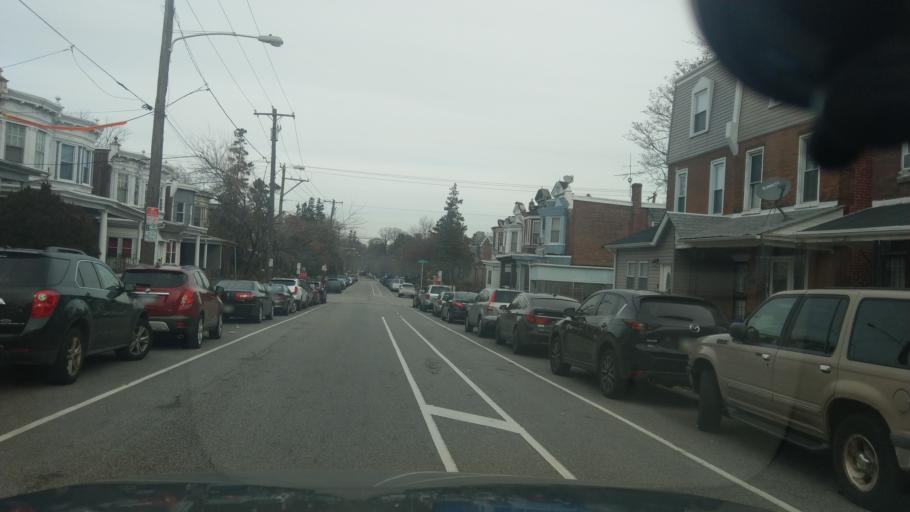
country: US
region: Pennsylvania
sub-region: Montgomery County
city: Wyncote
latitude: 40.0435
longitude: -75.1415
